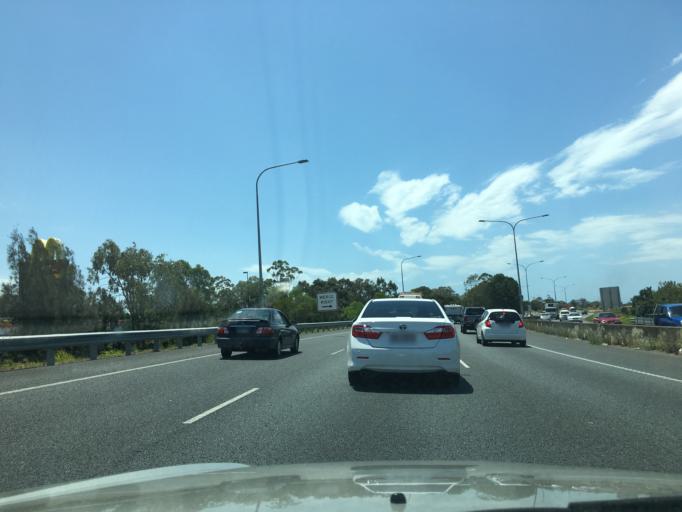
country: AU
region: Queensland
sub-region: Brisbane
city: Wavell Heights
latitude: -27.3787
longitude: 153.0941
